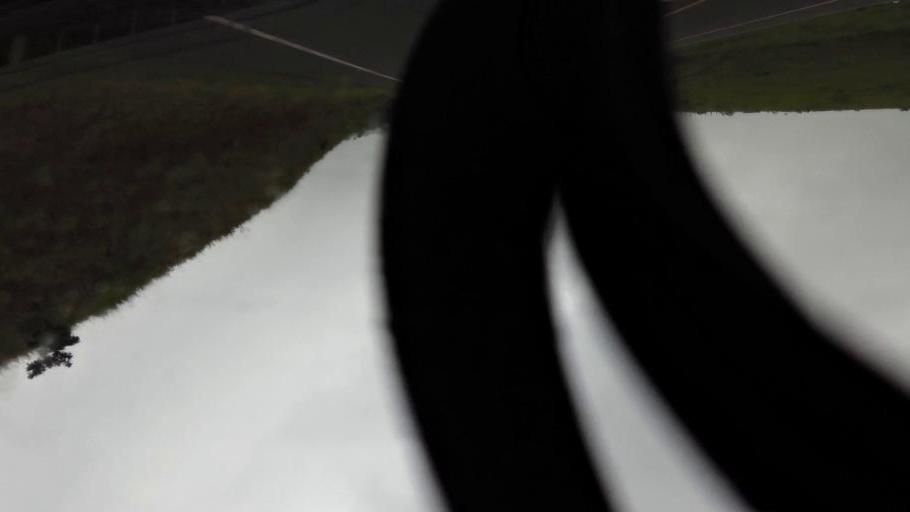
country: BR
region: Espirito Santo
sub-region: Guarapari
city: Guarapari
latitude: -20.6338
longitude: -40.5241
